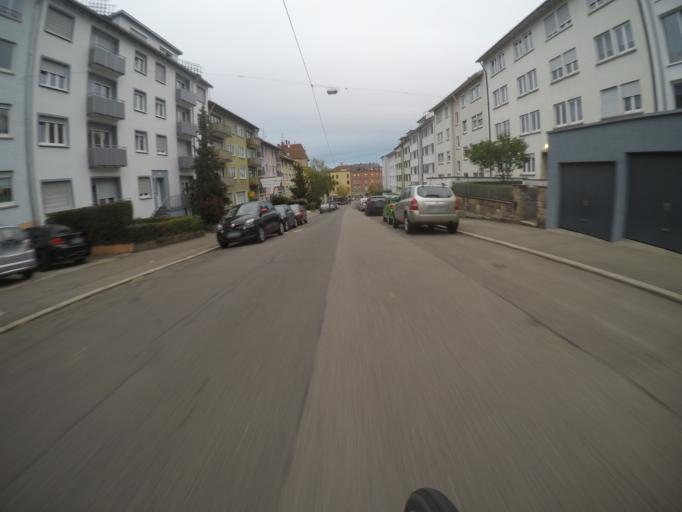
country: DE
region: Baden-Wuerttemberg
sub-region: Regierungsbezirk Stuttgart
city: Stuttgart-Ost
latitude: 48.7882
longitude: 9.1956
